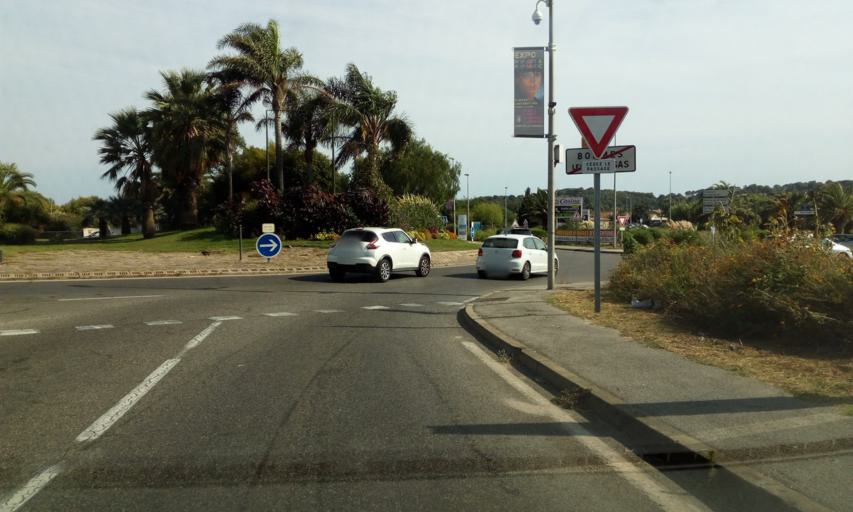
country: FR
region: Provence-Alpes-Cote d'Azur
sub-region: Departement du Var
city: Bormes-les-Mimosas
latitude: 43.1390
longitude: 6.3511
